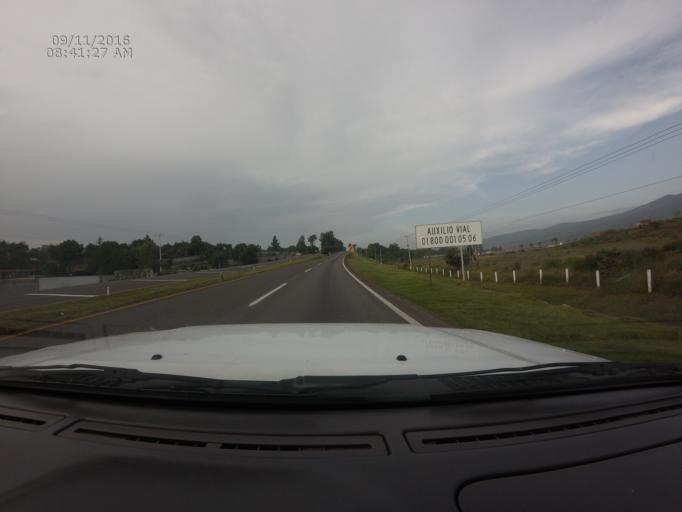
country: MX
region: Michoacan
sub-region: Morelia
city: La Mintzita (Piedra Dura)
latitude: 19.5988
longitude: -101.2917
